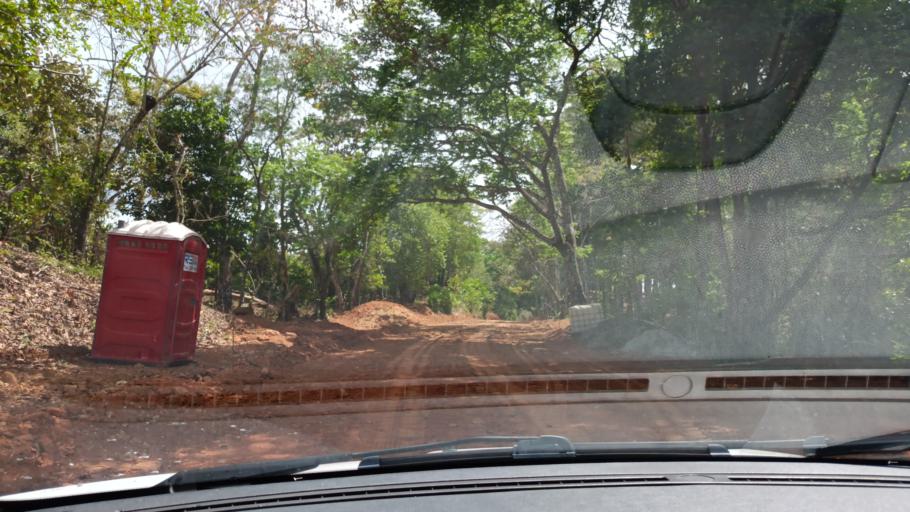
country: PA
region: Panama
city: La Cabima
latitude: 9.1235
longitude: -79.4960
